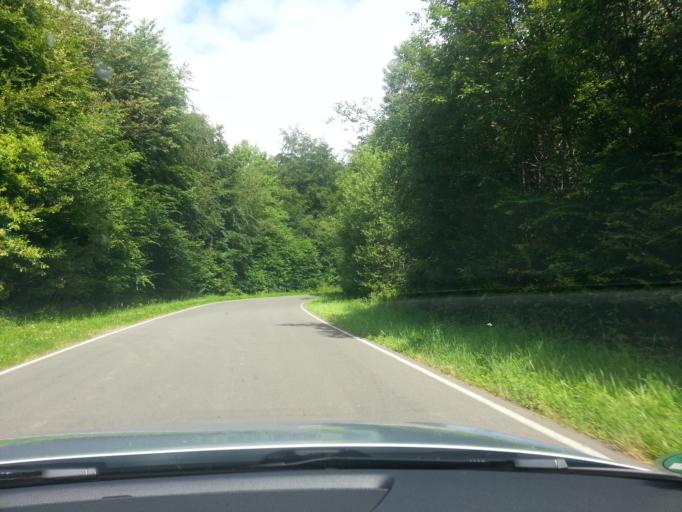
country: DE
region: Saarland
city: Orscholz
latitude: 49.5219
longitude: 6.5134
